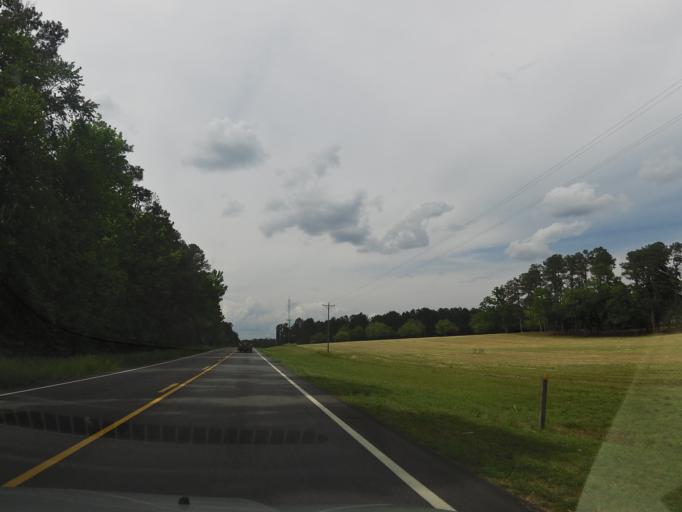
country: US
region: Georgia
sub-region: McDuffie County
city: Thomson
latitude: 33.4446
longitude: -82.4932
